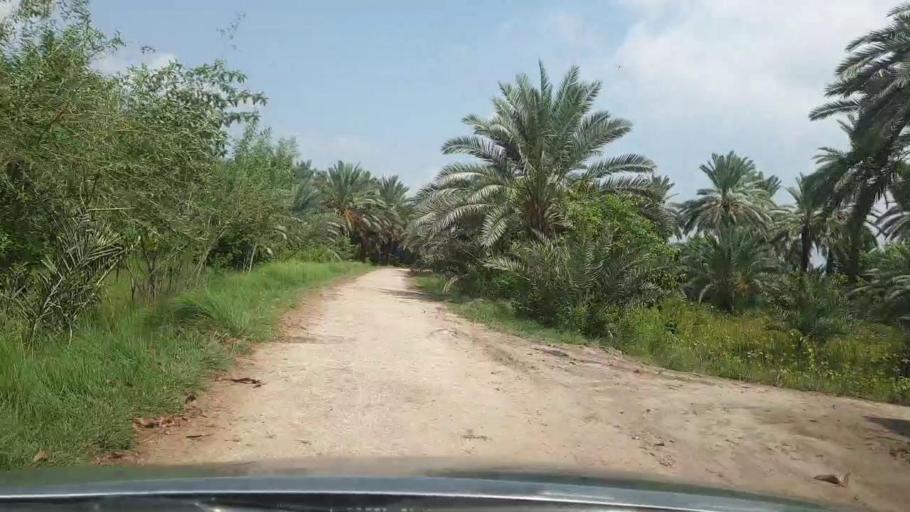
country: PK
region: Sindh
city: Pir jo Goth
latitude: 27.6149
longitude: 68.6666
